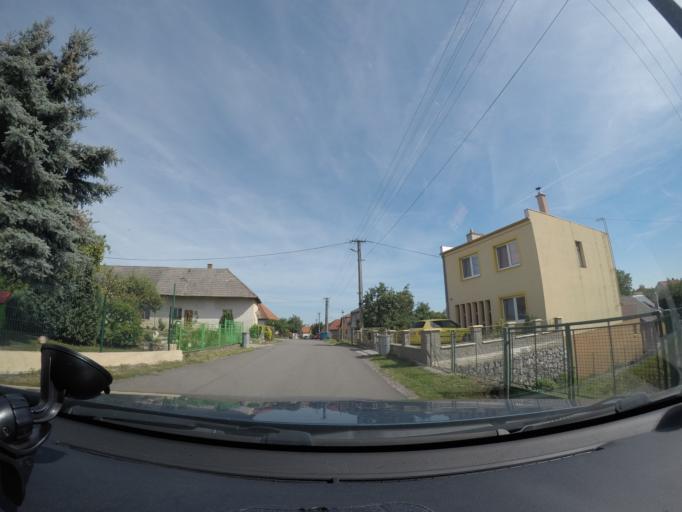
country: SK
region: Trenciansky
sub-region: Okres Trencin
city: Trencin
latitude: 48.7598
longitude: 18.1118
